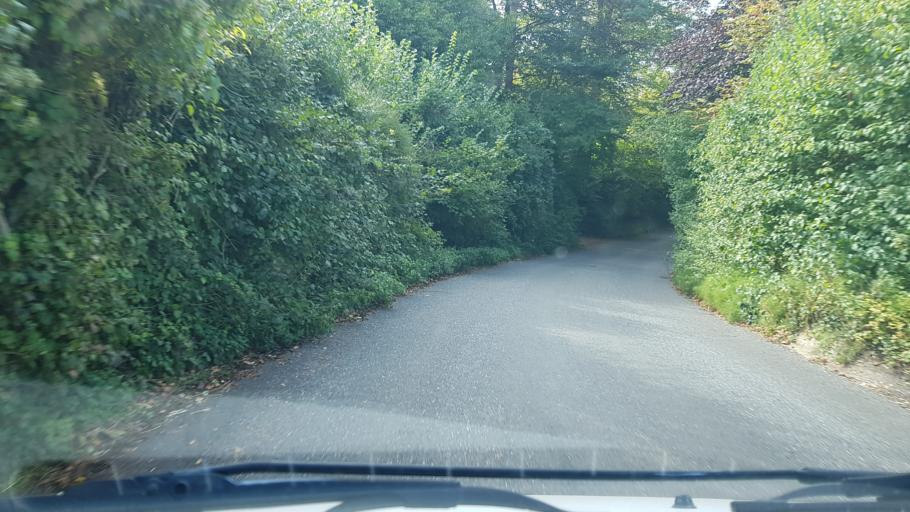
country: GB
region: England
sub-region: Surrey
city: Godalming
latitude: 51.2231
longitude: -0.6291
